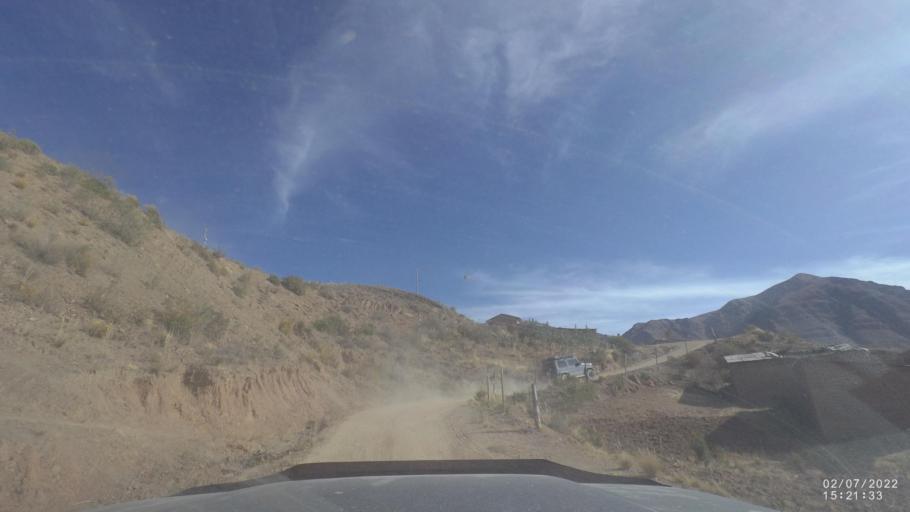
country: BO
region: Cochabamba
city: Irpa Irpa
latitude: -17.8718
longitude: -66.4237
